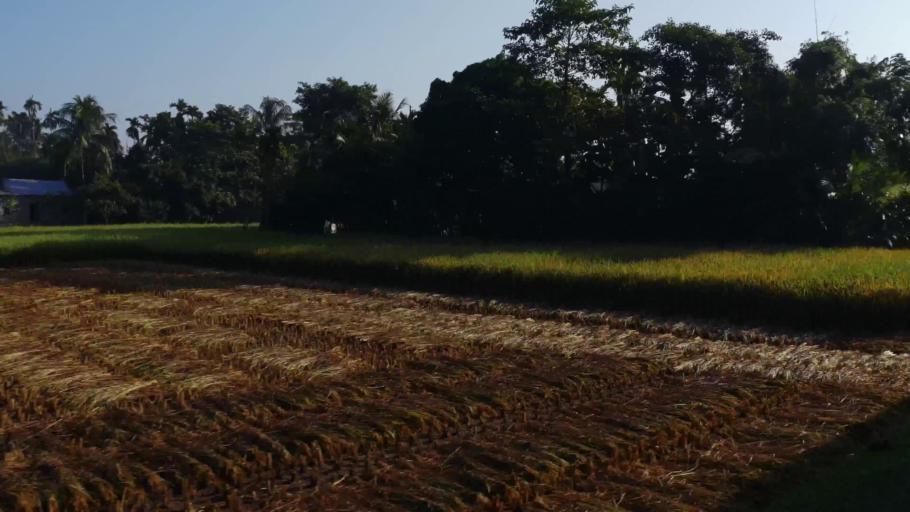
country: BD
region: Dhaka
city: Jamalpur
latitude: 24.8633
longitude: 90.0932
